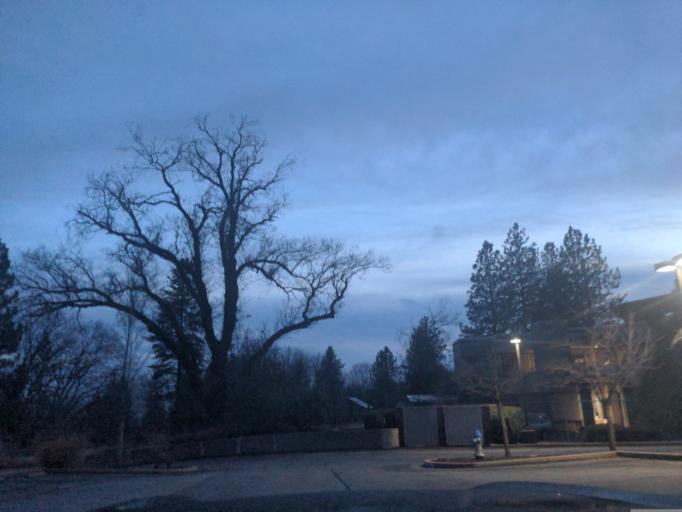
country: US
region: California
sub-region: Nevada County
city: Grass Valley
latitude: 39.2339
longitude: -121.0550
